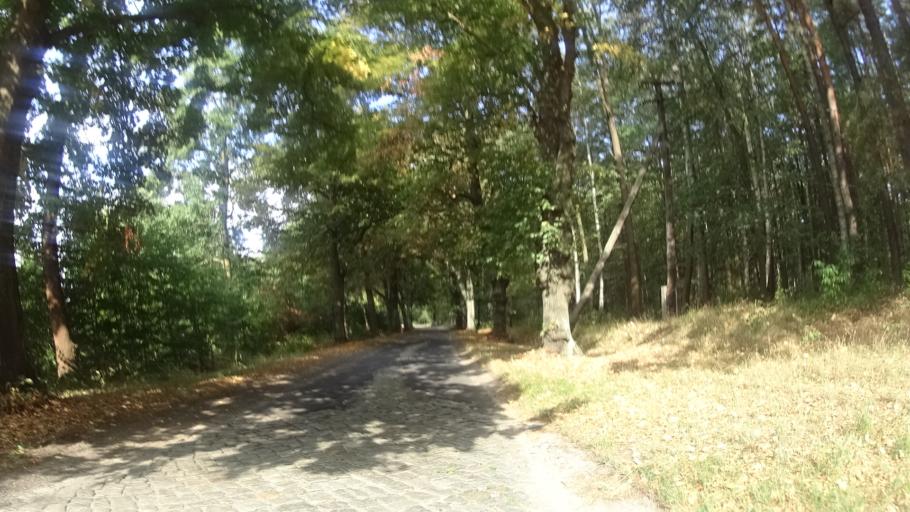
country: PL
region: Lubusz
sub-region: Powiat zarski
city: Przewoz
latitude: 51.4920
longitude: 14.8708
